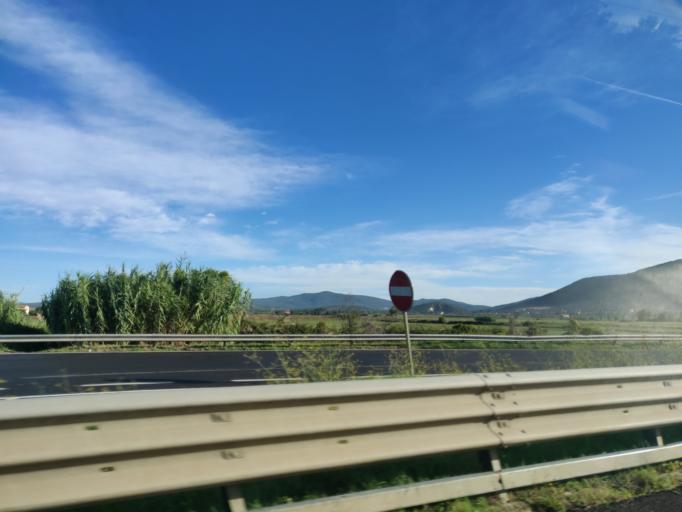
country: IT
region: Tuscany
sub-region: Provincia di Grosseto
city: Bagno Roselle
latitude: 42.7969
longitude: 11.1207
